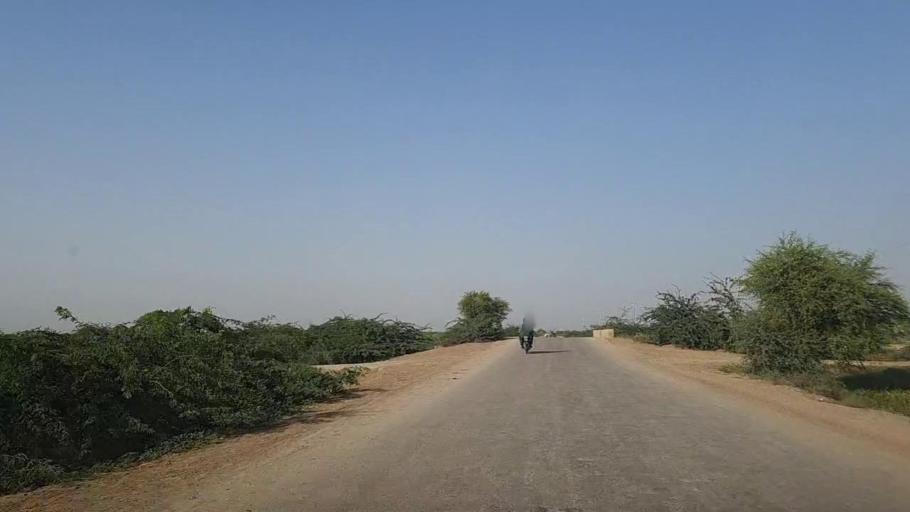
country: PK
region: Sindh
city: Mirpur Batoro
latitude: 24.5987
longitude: 68.4002
